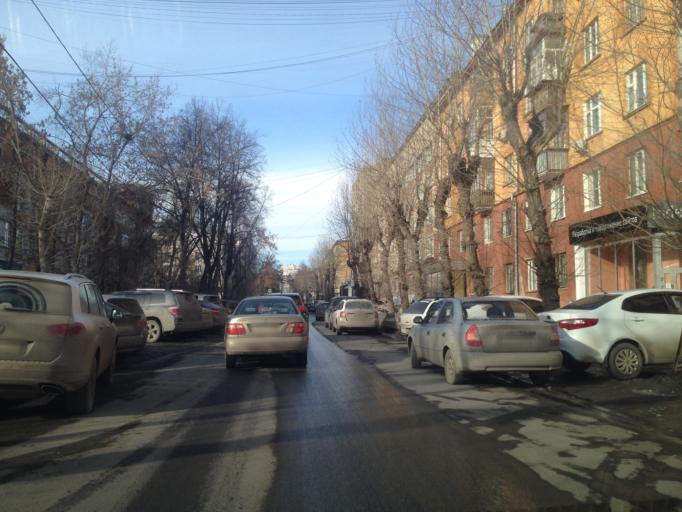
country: RU
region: Sverdlovsk
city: Yekaterinburg
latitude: 56.8419
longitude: 60.6256
